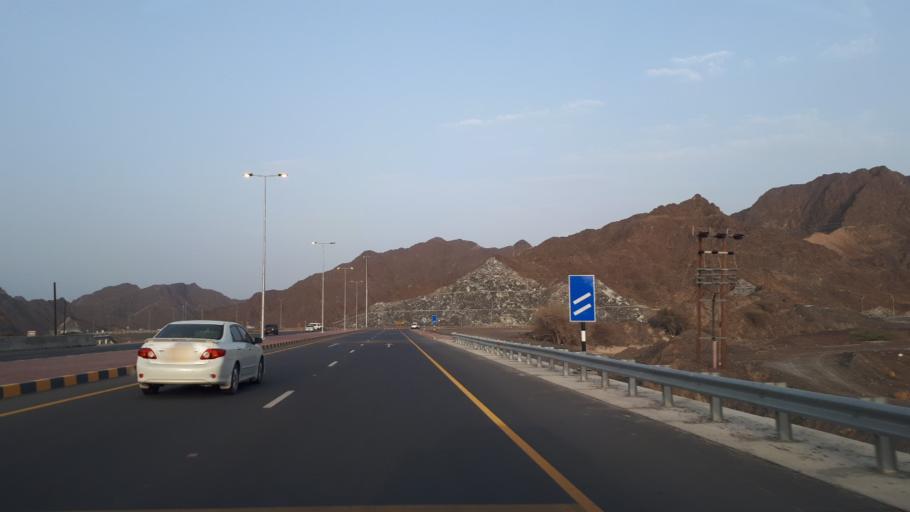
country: OM
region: Al Batinah
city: Rustaq
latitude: 23.4136
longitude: 57.3057
